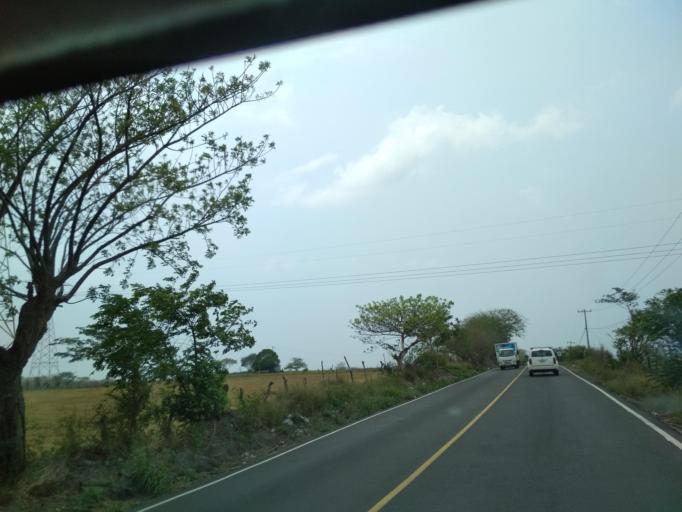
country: MX
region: Veracruz
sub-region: Veracruz
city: Delfino Victoria (Santa Fe)
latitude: 19.1578
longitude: -96.2871
